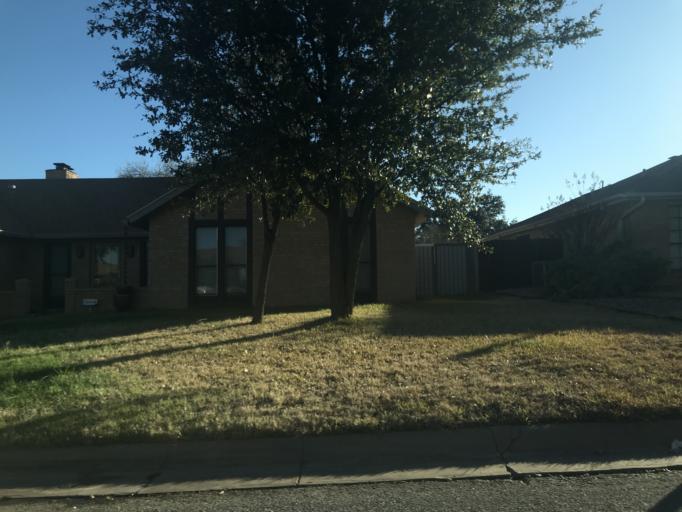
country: US
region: Texas
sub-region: Tom Green County
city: San Angelo
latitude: 31.4266
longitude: -100.4929
